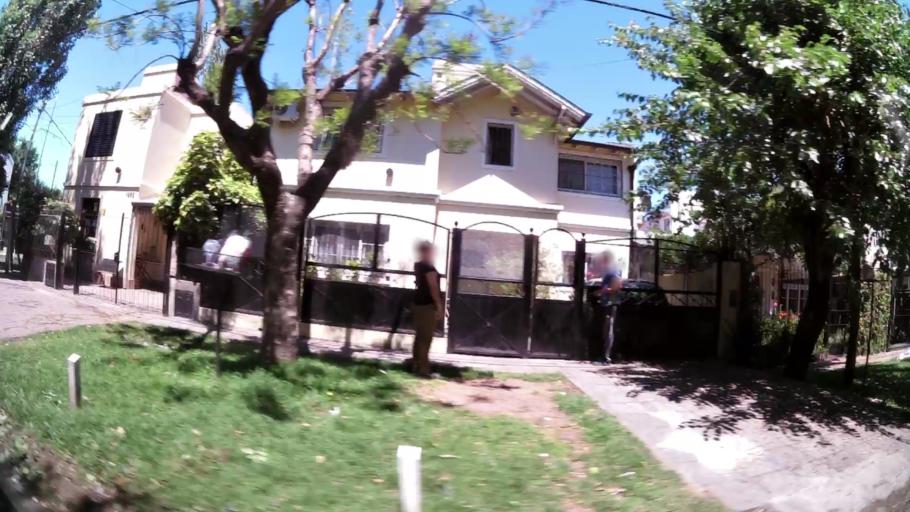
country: AR
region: Buenos Aires
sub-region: Partido de Tigre
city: Tigre
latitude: -34.4923
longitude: -58.6306
